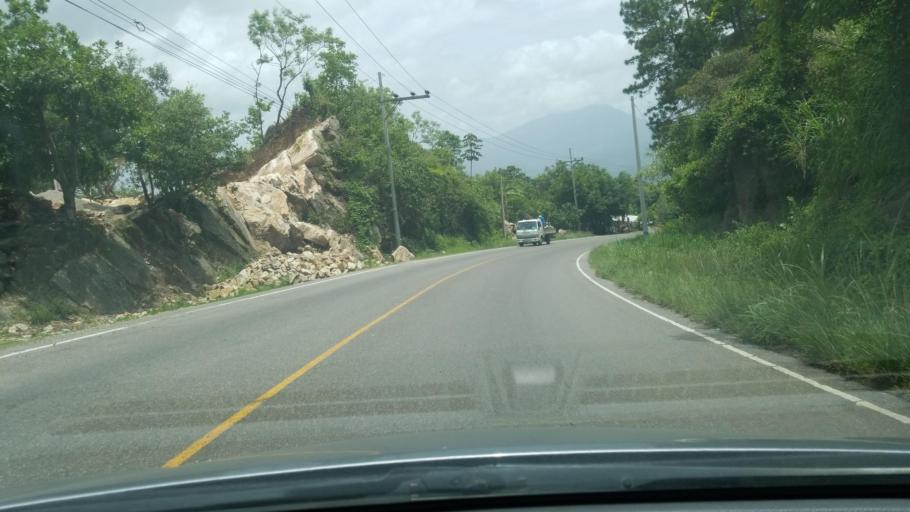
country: HN
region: Copan
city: Ojos de Agua
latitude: 14.6808
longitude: -88.8191
